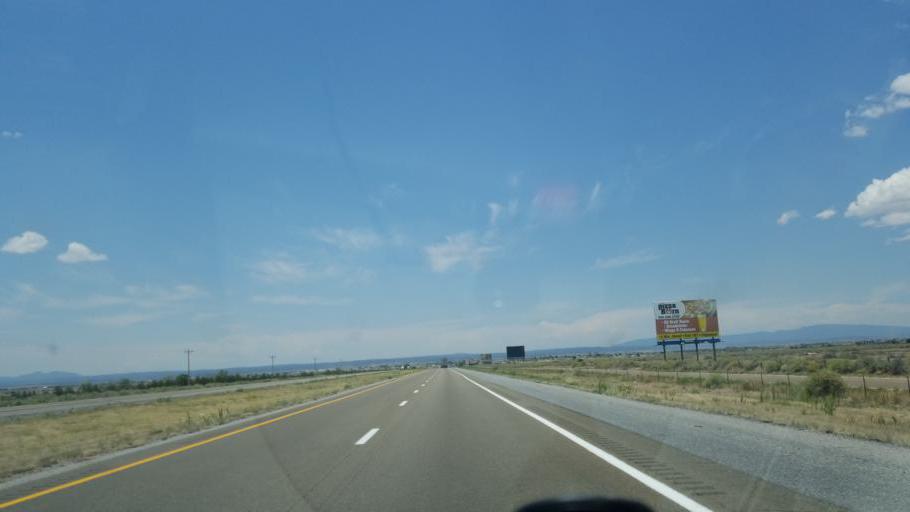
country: US
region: New Mexico
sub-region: Torrance County
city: Moriarty
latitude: 35.0049
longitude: -105.9814
